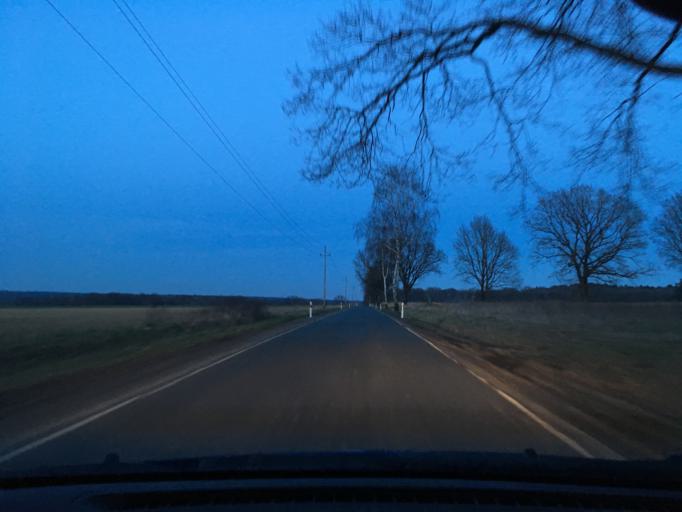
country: DE
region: Lower Saxony
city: Eyendorf
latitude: 53.2015
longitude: 10.1717
